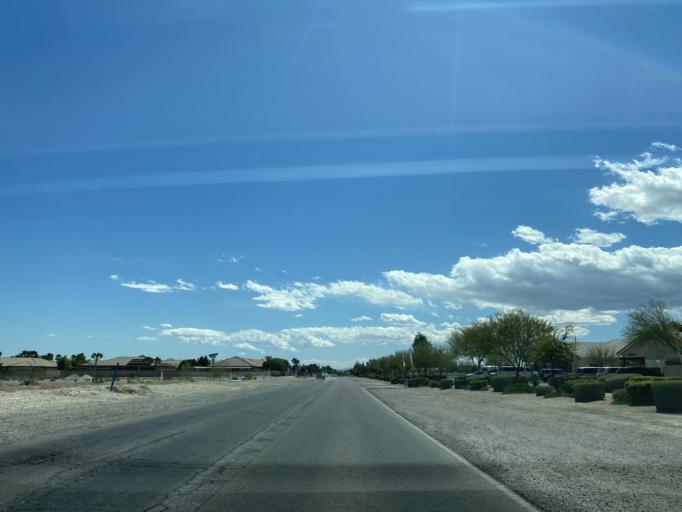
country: US
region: Nevada
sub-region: Clark County
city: North Las Vegas
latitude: 36.3040
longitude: -115.2422
